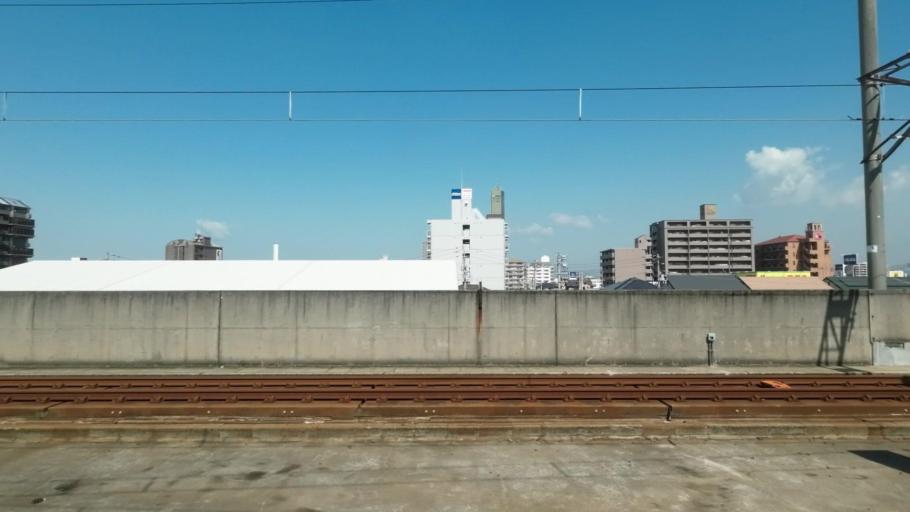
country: JP
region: Kagawa
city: Sakaidecho
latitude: 34.3079
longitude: 133.8149
